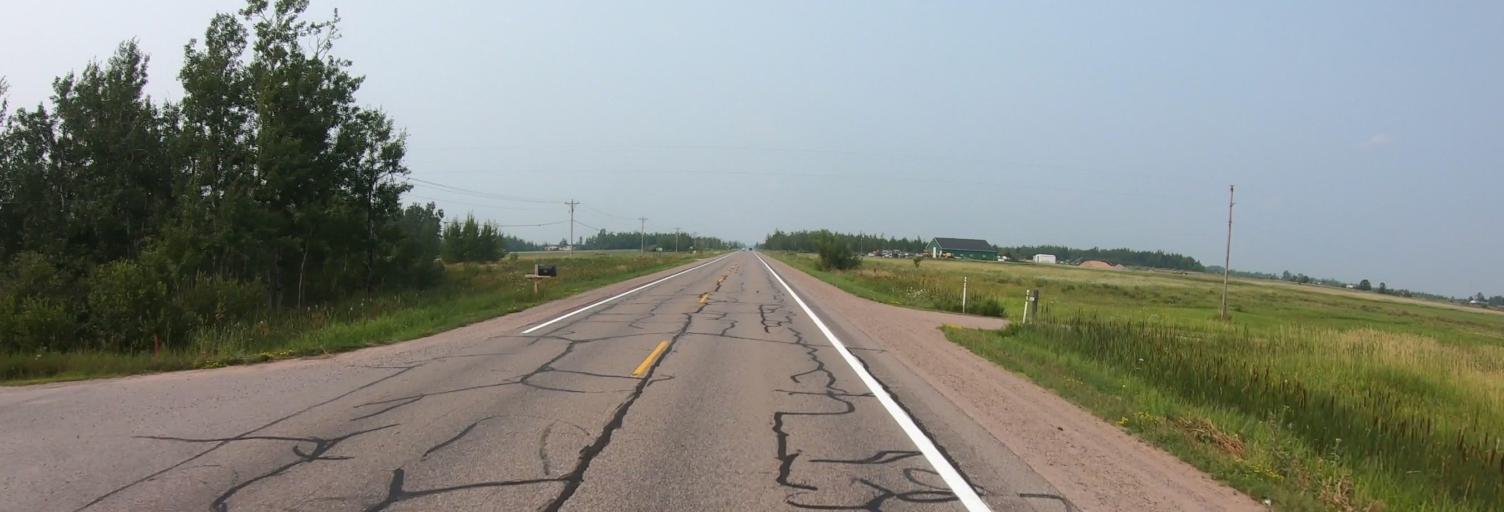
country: US
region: Michigan
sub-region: Chippewa County
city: Sault Ste. Marie
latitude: 46.4212
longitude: -84.3534
